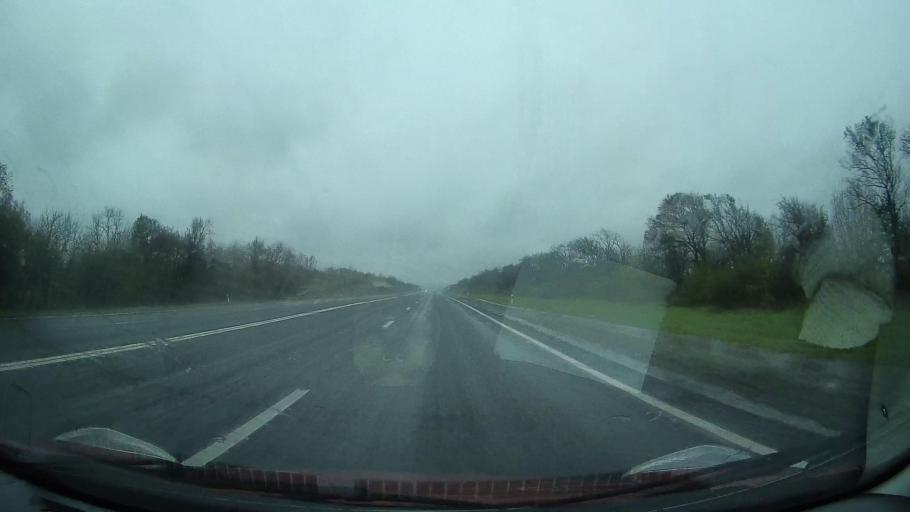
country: RU
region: Stavropol'skiy
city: Nevinnomyssk
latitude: 44.6160
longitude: 42.1055
